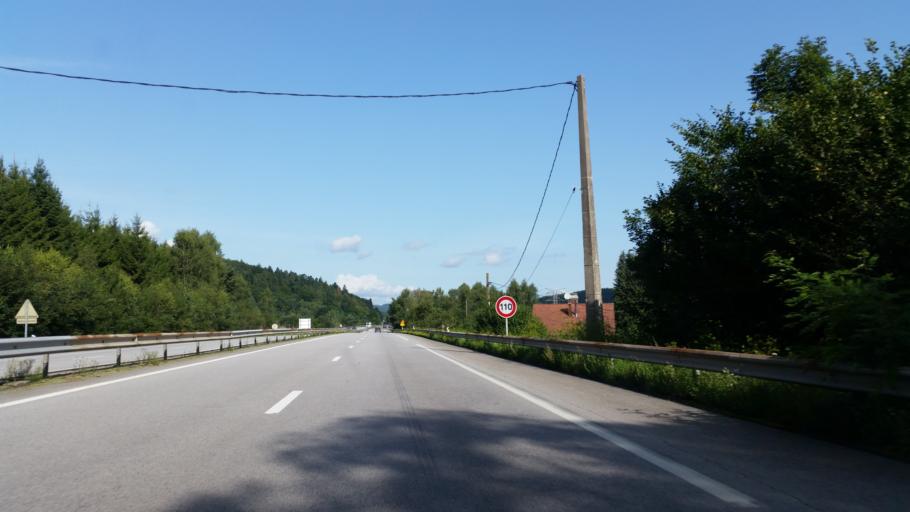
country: FR
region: Lorraine
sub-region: Departement des Vosges
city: Eloyes
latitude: 48.0920
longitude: 6.5953
